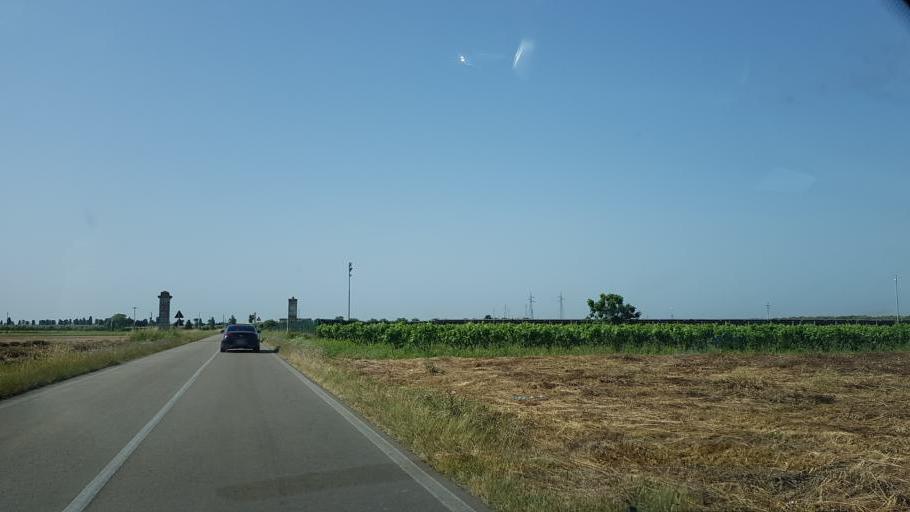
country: IT
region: Apulia
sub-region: Provincia di Brindisi
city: San Pancrazio Salentino
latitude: 40.3940
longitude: 17.8348
